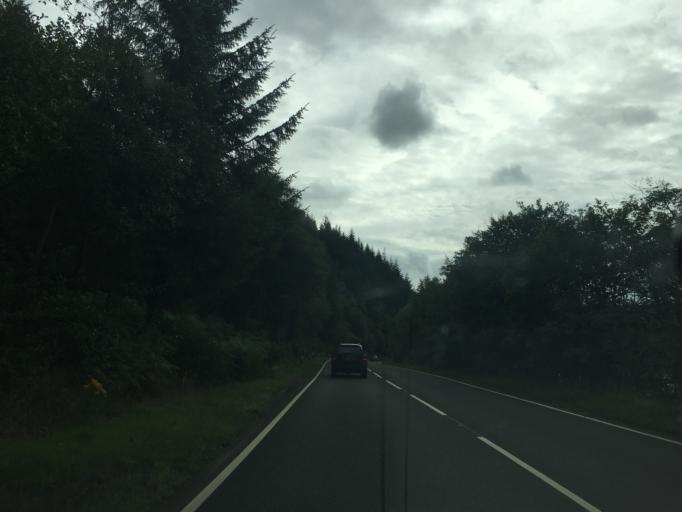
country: GB
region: Scotland
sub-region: Stirling
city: Callander
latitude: 56.2831
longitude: -4.2844
